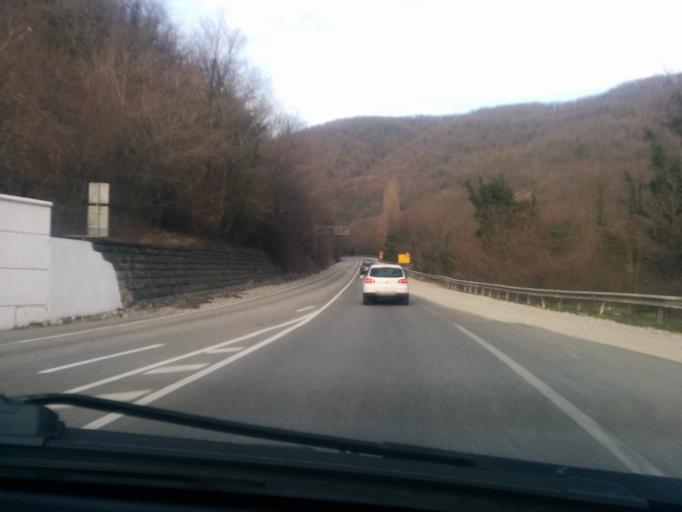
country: RU
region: Krasnodarskiy
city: Agoy
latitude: 44.1409
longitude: 39.0509
